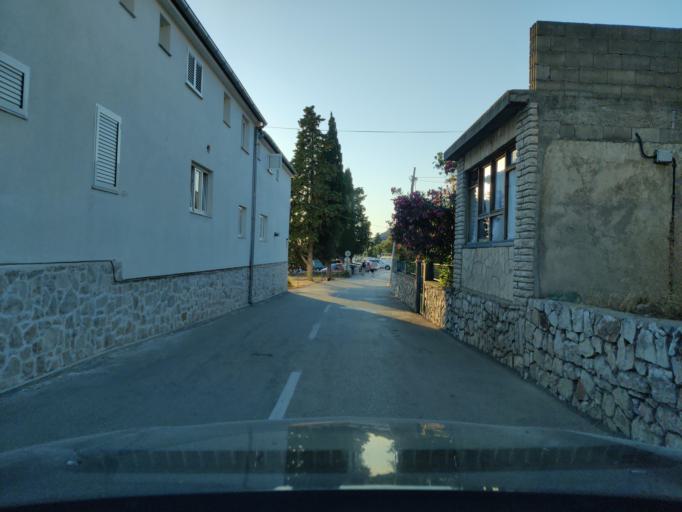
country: HR
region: Sibensko-Kniniska
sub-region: Grad Sibenik
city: Tisno
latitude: 43.8031
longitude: 15.6352
